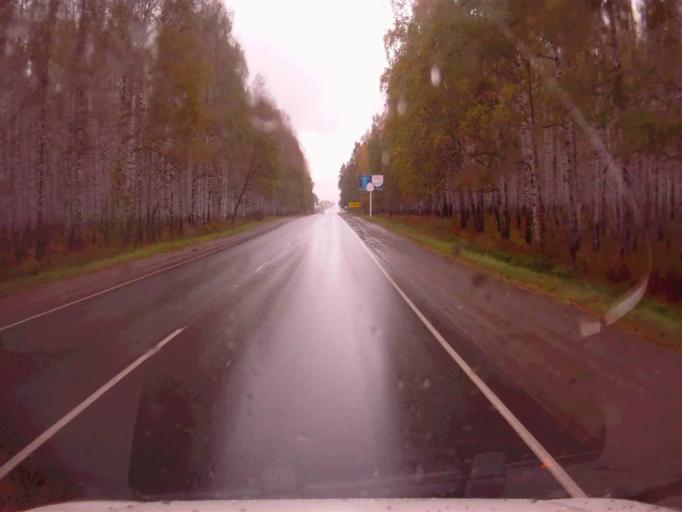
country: RU
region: Chelyabinsk
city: Argayash
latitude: 55.4139
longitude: 61.0344
